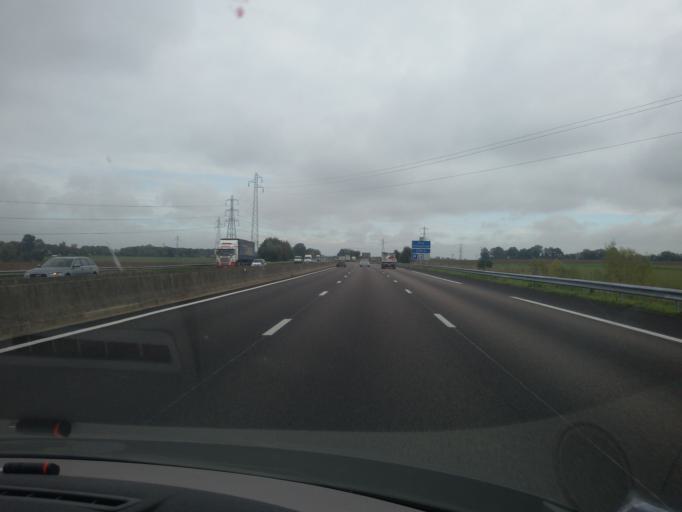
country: FR
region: Haute-Normandie
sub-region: Departement de l'Eure
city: Corneville-sur-Risle
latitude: 49.3719
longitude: 0.6687
